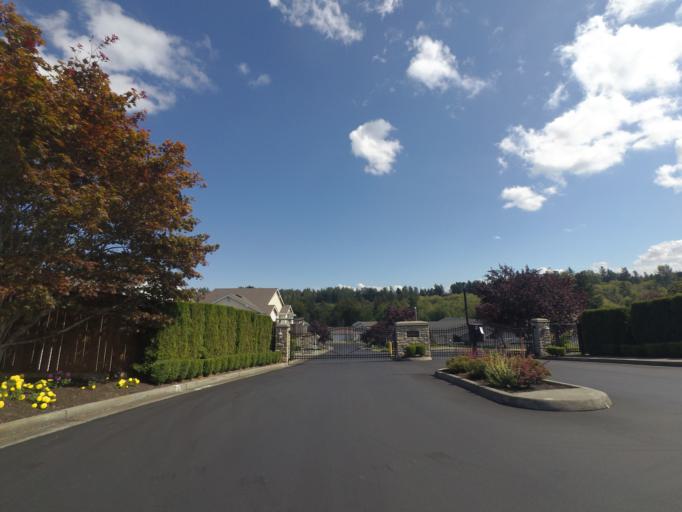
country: US
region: Washington
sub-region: Pierce County
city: Fircrest
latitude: 47.2082
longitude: -122.5158
